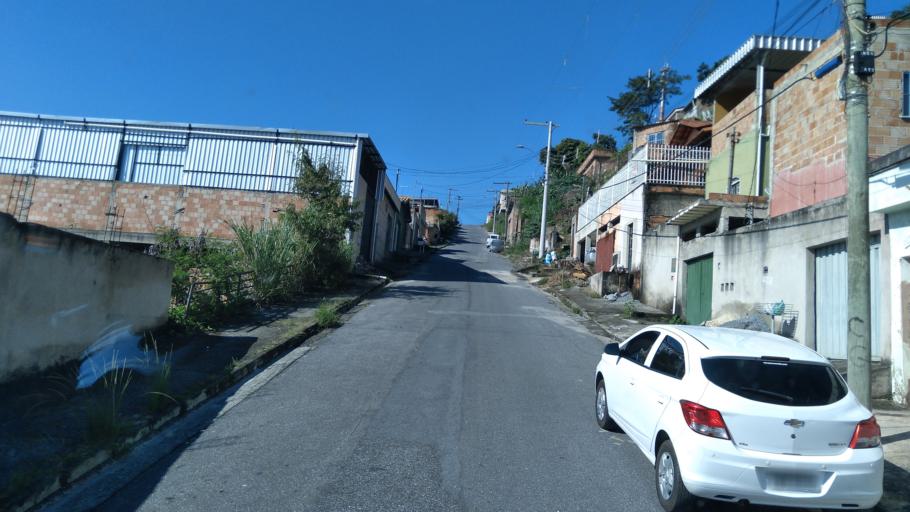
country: BR
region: Minas Gerais
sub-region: Santa Luzia
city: Santa Luzia
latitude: -19.8283
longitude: -43.8969
